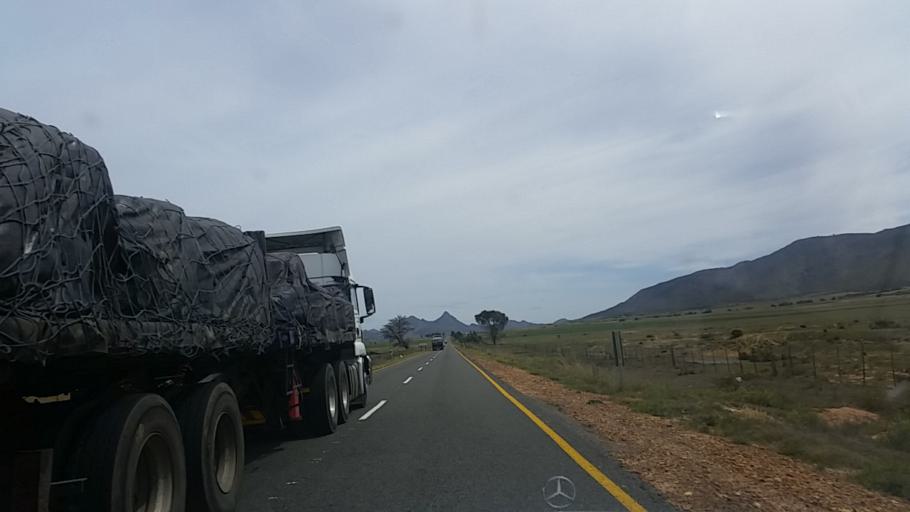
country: ZA
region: Western Cape
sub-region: Eden District Municipality
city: George
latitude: -33.8122
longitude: 22.5330
